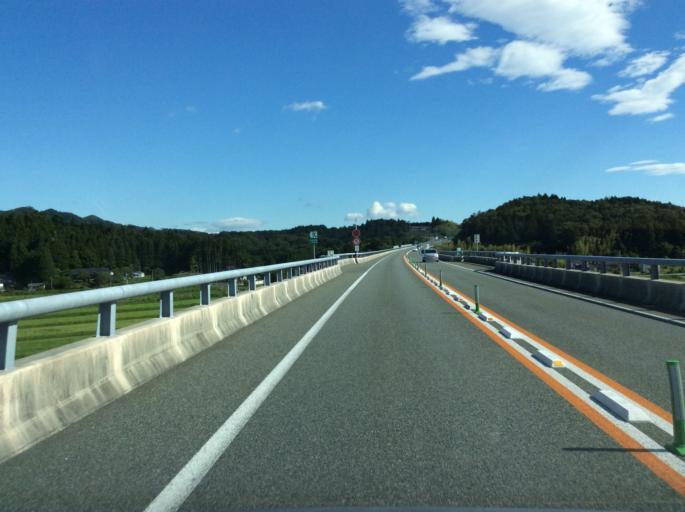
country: JP
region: Fukushima
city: Namie
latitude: 37.2796
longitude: 140.9815
